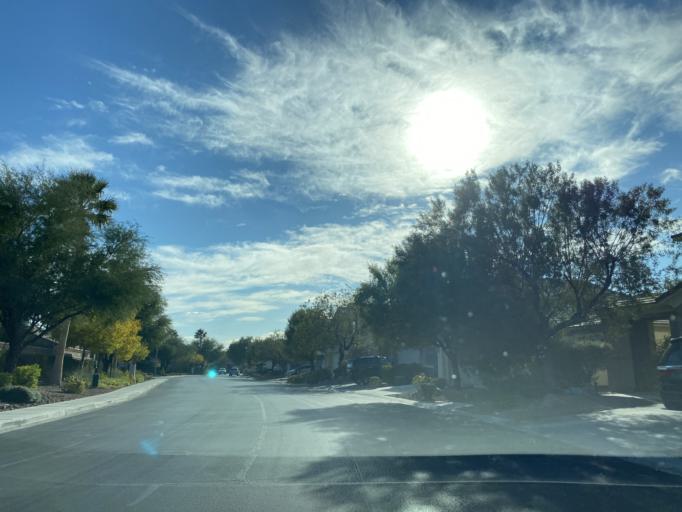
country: US
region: Nevada
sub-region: Clark County
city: North Las Vegas
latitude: 36.3170
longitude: -115.2436
